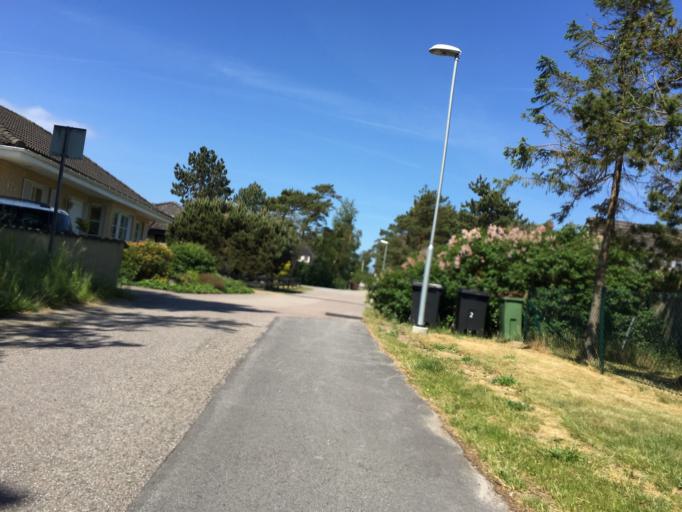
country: SE
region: Skane
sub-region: Trelleborgs Kommun
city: Anderslov
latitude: 55.3463
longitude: 13.2742
